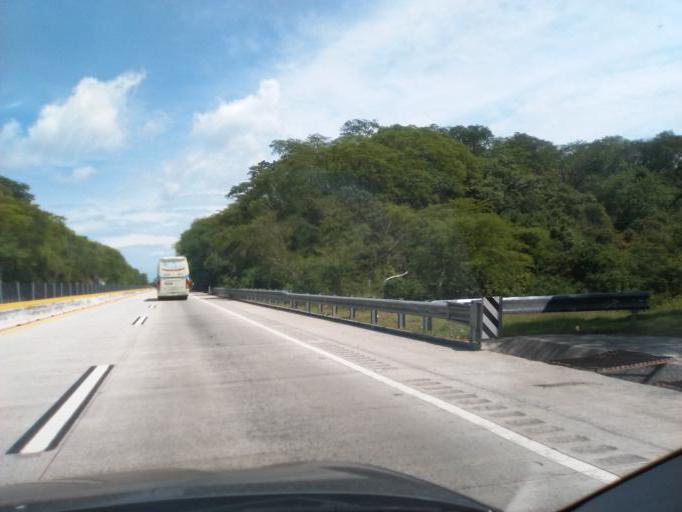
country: MX
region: Guerrero
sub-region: Acapulco de Juarez
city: Colonia Nueva Revolucion
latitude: 16.9305
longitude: -99.7884
